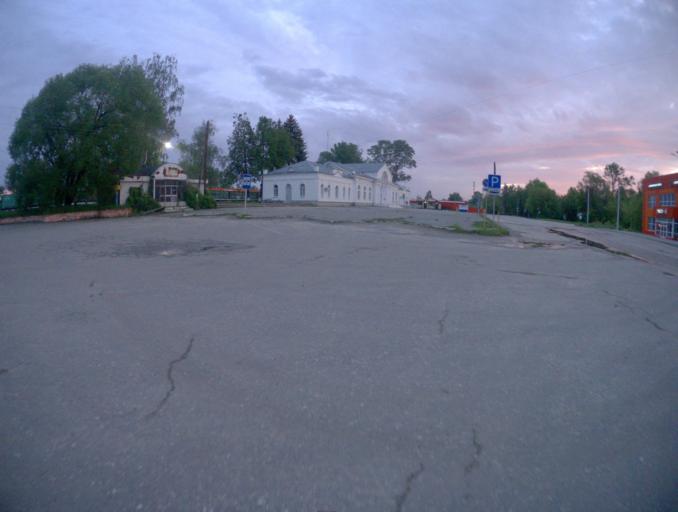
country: RU
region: Vladimir
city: Gus'-Khrustal'nyy
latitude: 55.6180
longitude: 40.6512
